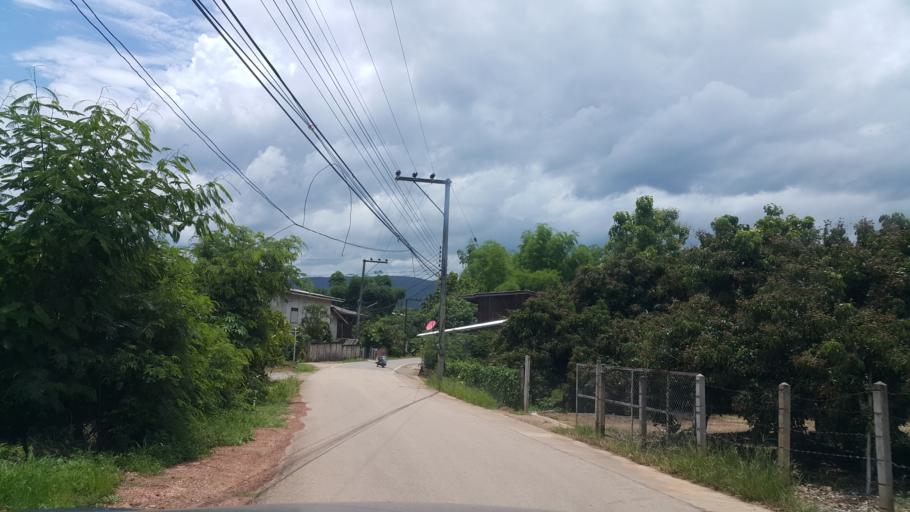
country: TH
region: Chiang Mai
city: Mae Taeng
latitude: 19.1966
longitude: 99.0015
